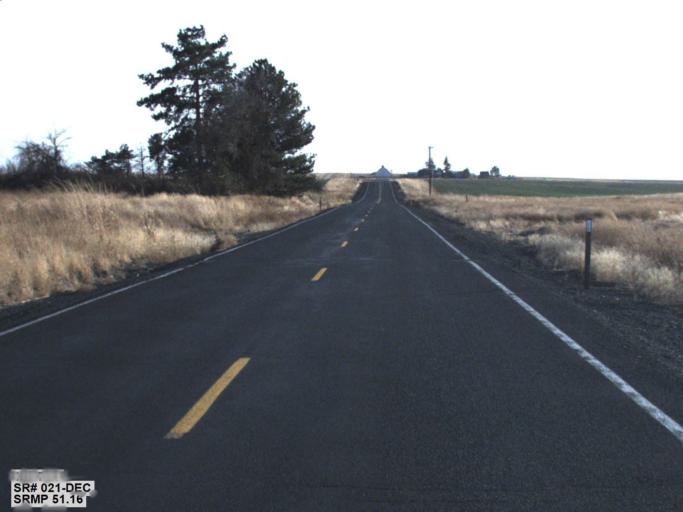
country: US
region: Washington
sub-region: Adams County
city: Ritzville
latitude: 47.2700
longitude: -118.6911
